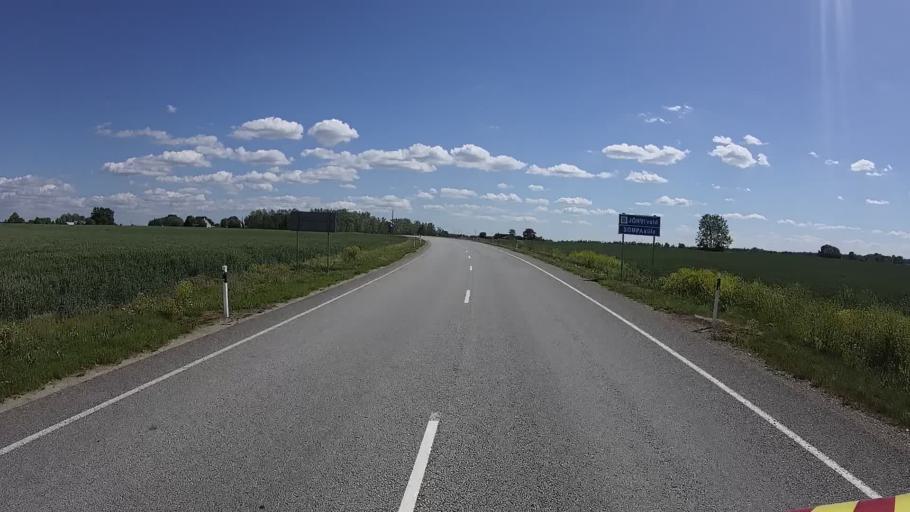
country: EE
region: Ida-Virumaa
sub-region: Johvi vald
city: Johvi
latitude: 59.3723
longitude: 27.3492
